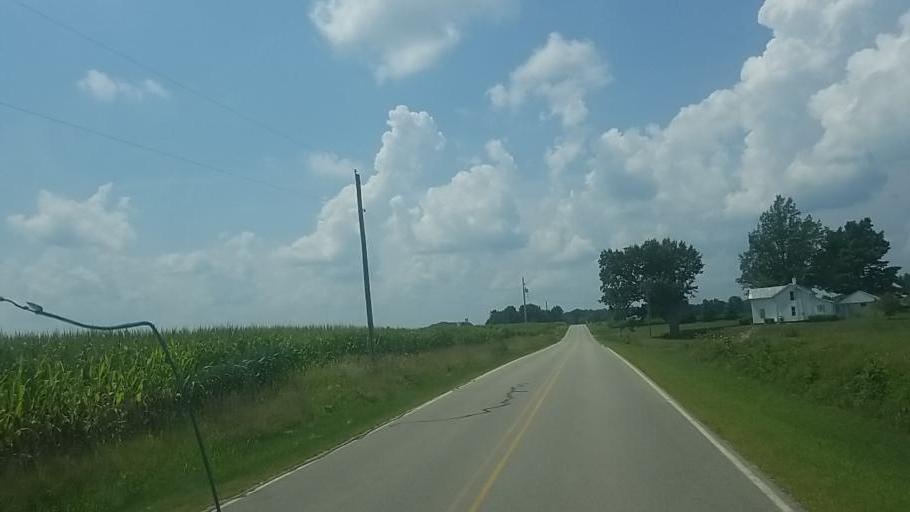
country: US
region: Ohio
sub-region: Crawford County
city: Bucyrus
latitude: 40.7667
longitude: -83.0445
